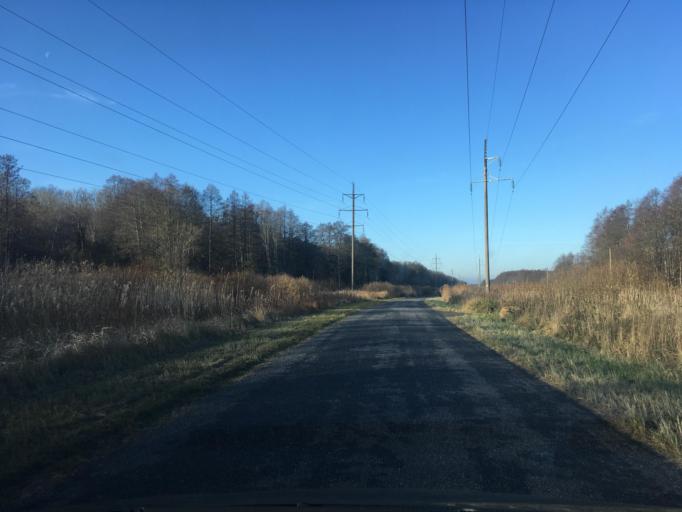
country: EE
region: Harju
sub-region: Maardu linn
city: Maardu
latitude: 59.4787
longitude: 25.1110
